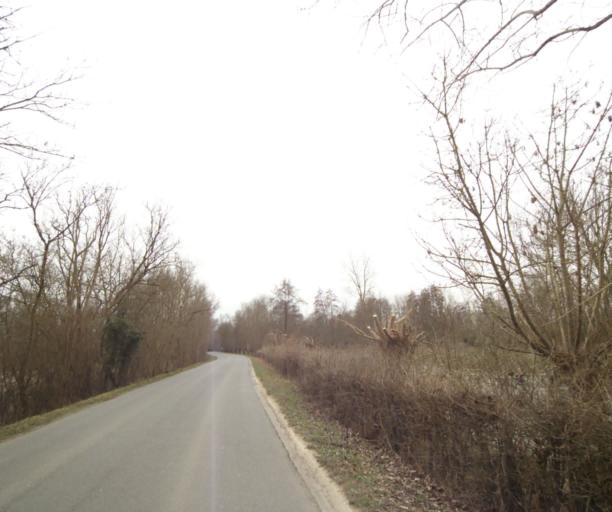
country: FR
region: Poitou-Charentes
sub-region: Departement des Deux-Sevres
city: Bessines
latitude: 46.3055
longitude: -0.5163
